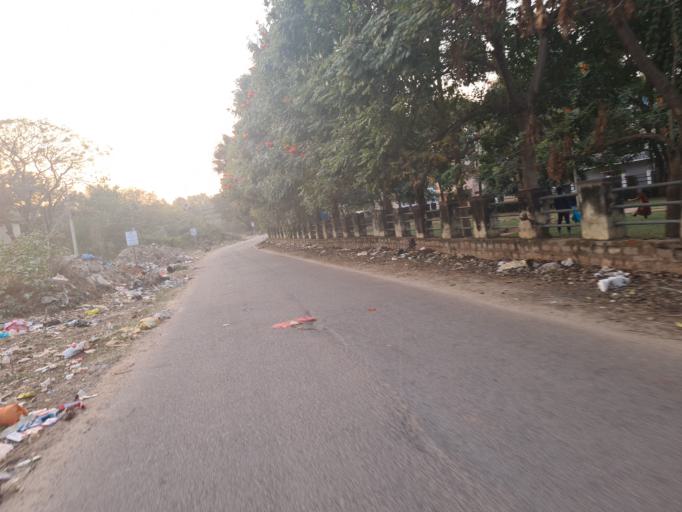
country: IN
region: Telangana
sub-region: Medak
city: Serilingampalle
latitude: 17.4785
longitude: 78.2972
